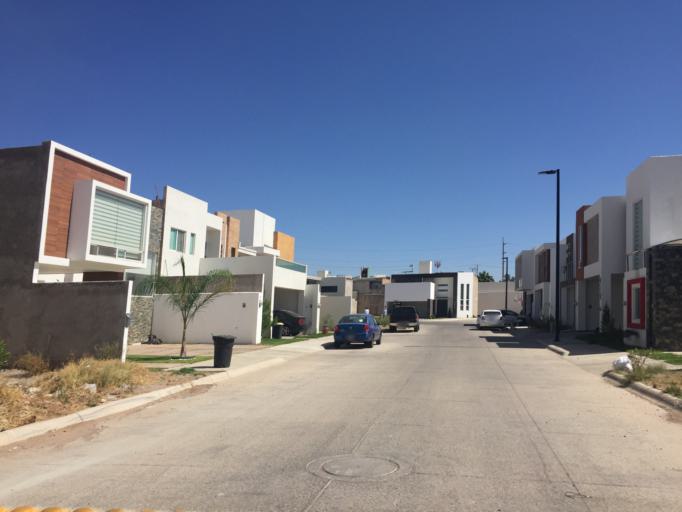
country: MX
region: Durango
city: Victoria de Durango
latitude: 24.0020
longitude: -104.6360
